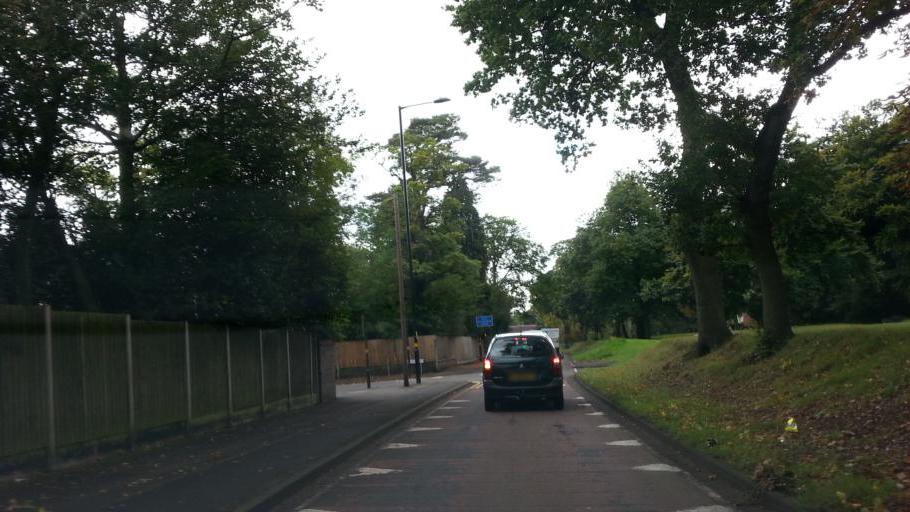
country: GB
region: England
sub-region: Sandwell
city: Smethwick
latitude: 52.4556
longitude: -1.9543
